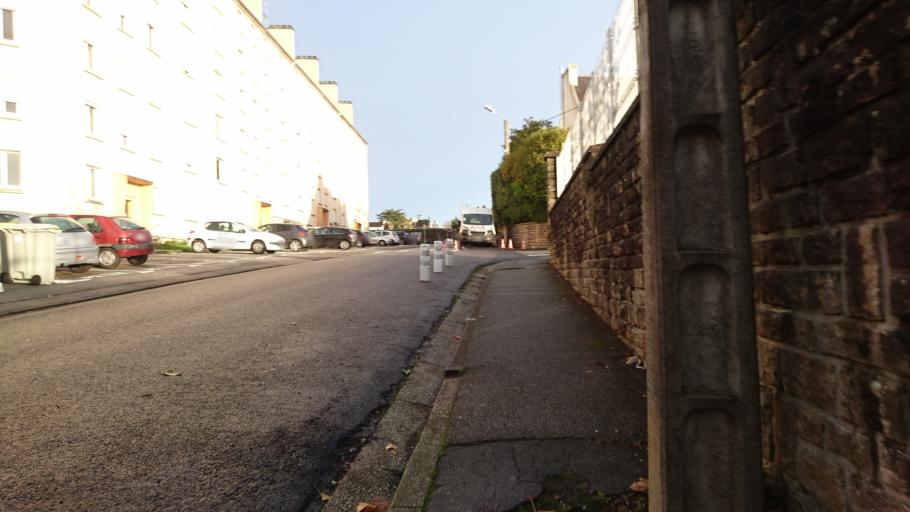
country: FR
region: Brittany
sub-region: Departement du Finistere
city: Quimper
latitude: 47.9997
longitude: -4.0993
